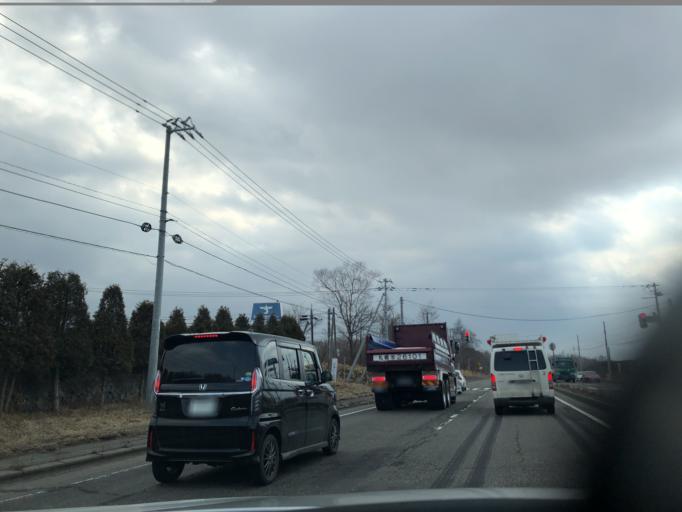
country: JP
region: Hokkaido
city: Chitose
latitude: 42.7749
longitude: 141.7056
